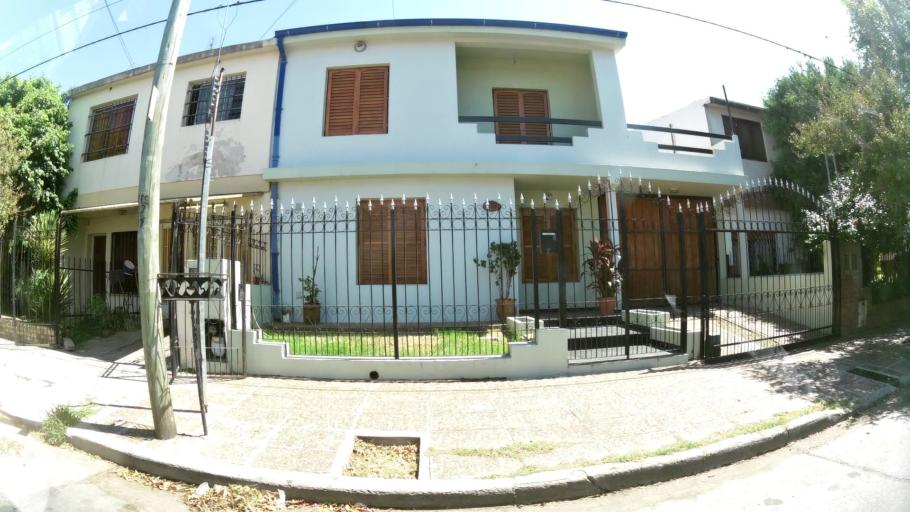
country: AR
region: Cordoba
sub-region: Departamento de Capital
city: Cordoba
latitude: -31.4531
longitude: -64.1631
